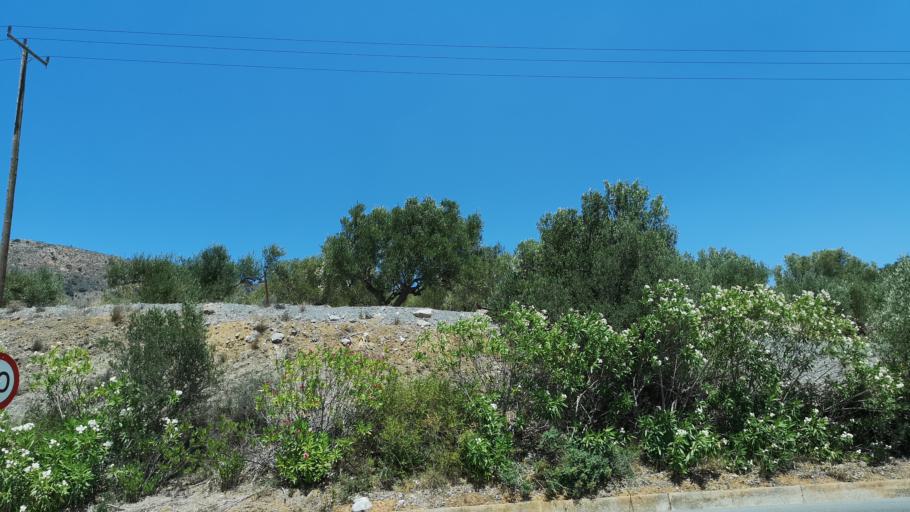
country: GR
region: Crete
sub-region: Nomos Lasithiou
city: Neapoli
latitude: 35.2370
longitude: 25.6480
